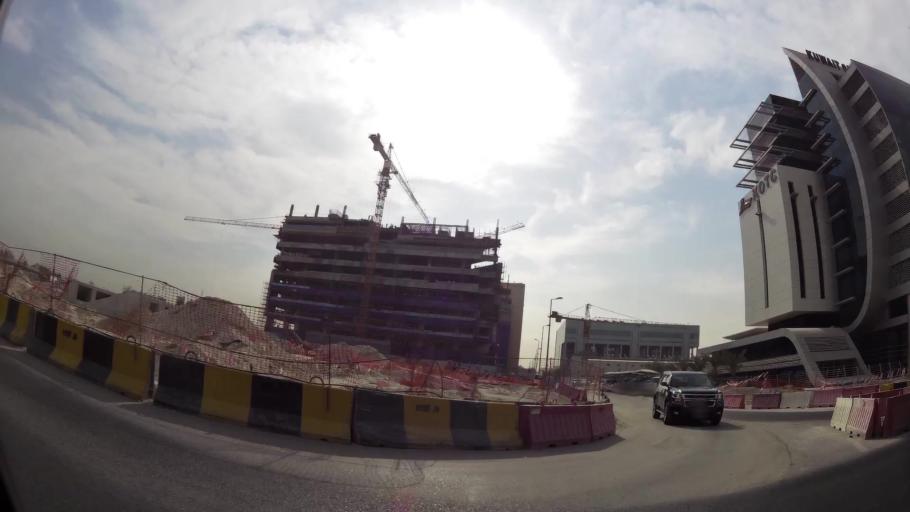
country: KW
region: Al Asimah
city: Ash Shamiyah
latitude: 29.3497
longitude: 47.9427
